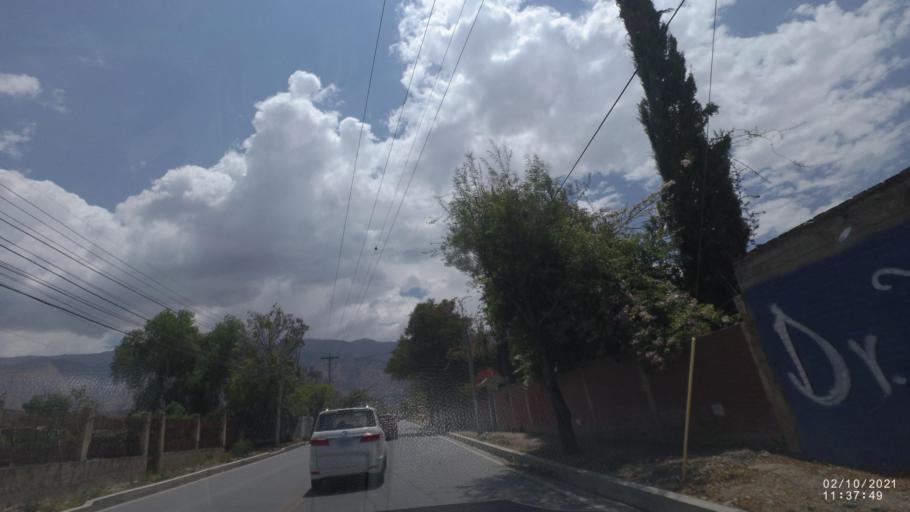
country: BO
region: Cochabamba
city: Cochabamba
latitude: -17.3426
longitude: -66.2226
